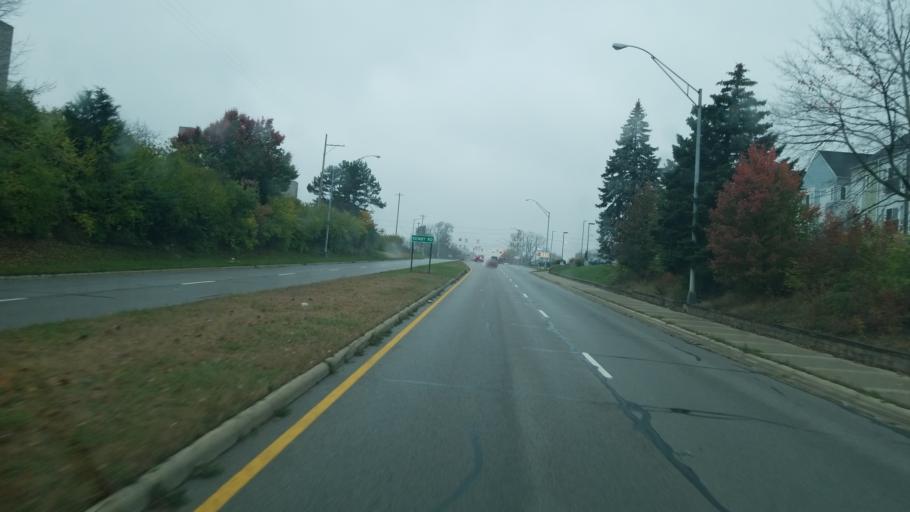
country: US
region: Ohio
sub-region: Franklin County
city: Worthington
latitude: 40.0530
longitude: -83.0463
